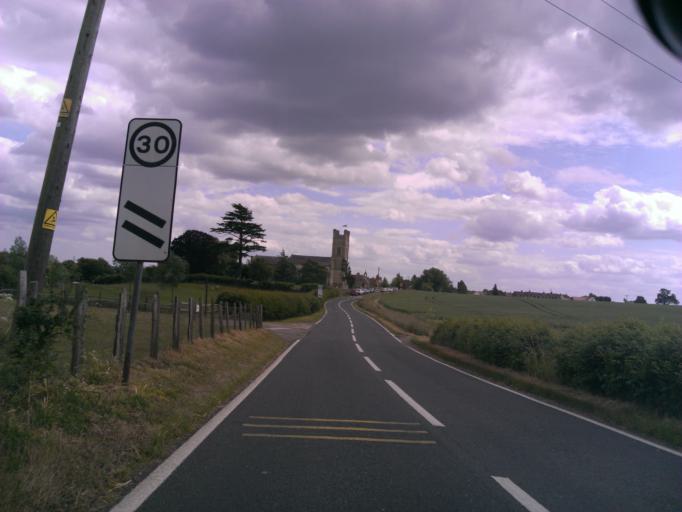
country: GB
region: England
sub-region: Essex
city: Witham
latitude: 51.8309
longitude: 0.6500
